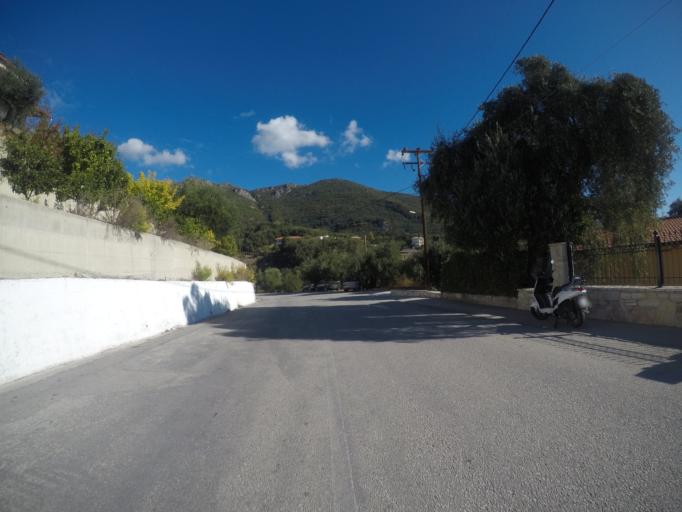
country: GR
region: Epirus
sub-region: Nomos Prevezis
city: Parga
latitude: 39.2874
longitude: 20.3963
